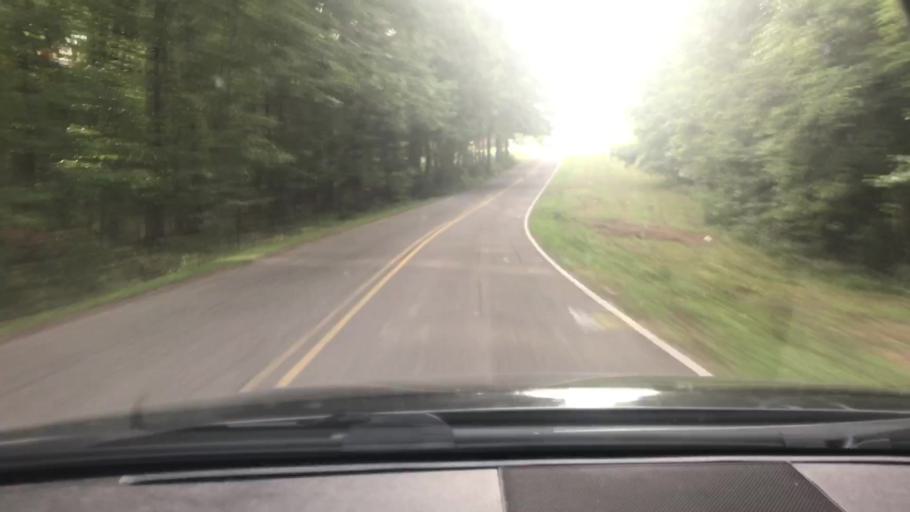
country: US
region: Tennessee
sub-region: Dickson County
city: White Bluff
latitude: 36.1703
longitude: -87.2631
